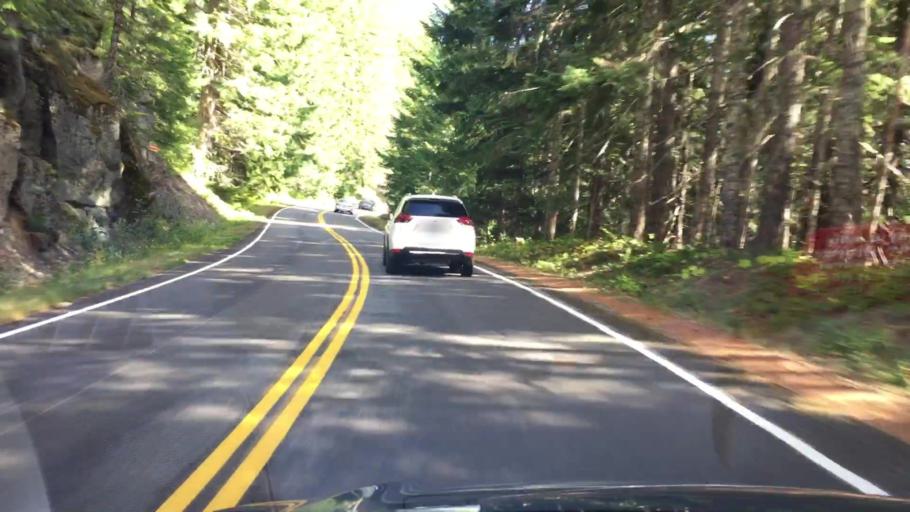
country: US
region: Washington
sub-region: Pierce County
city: Buckley
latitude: 46.7342
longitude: -121.6144
